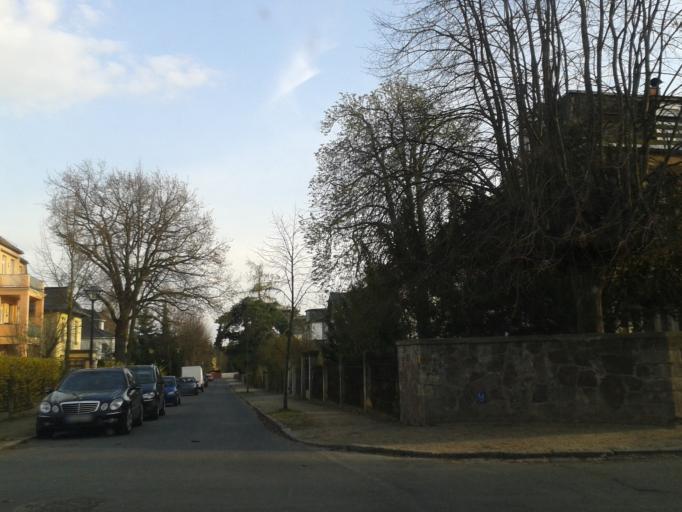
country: DE
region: Saxony
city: Radebeul
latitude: 51.1074
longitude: 13.6826
